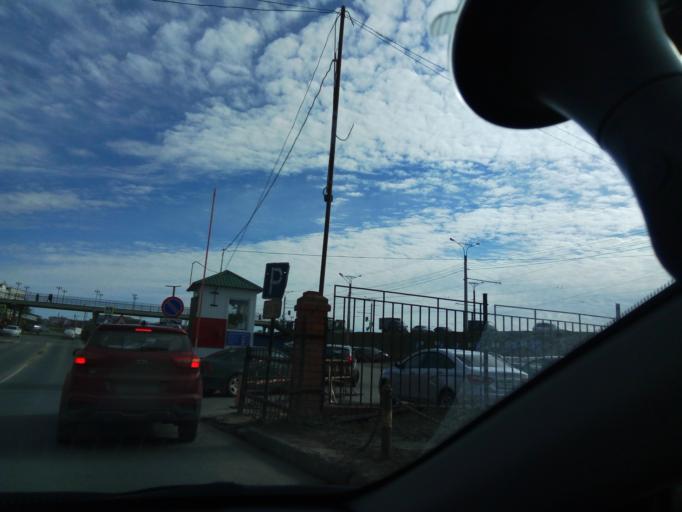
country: RU
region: Chuvashia
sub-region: Cheboksarskiy Rayon
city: Cheboksary
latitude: 56.1237
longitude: 47.2460
